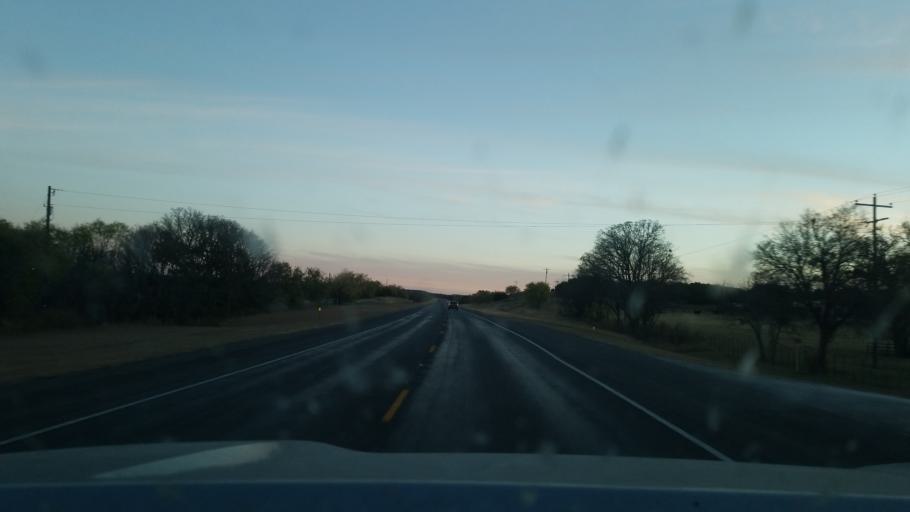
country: US
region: Texas
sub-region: Stephens County
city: Breckenridge
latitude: 32.5968
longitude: -98.8994
